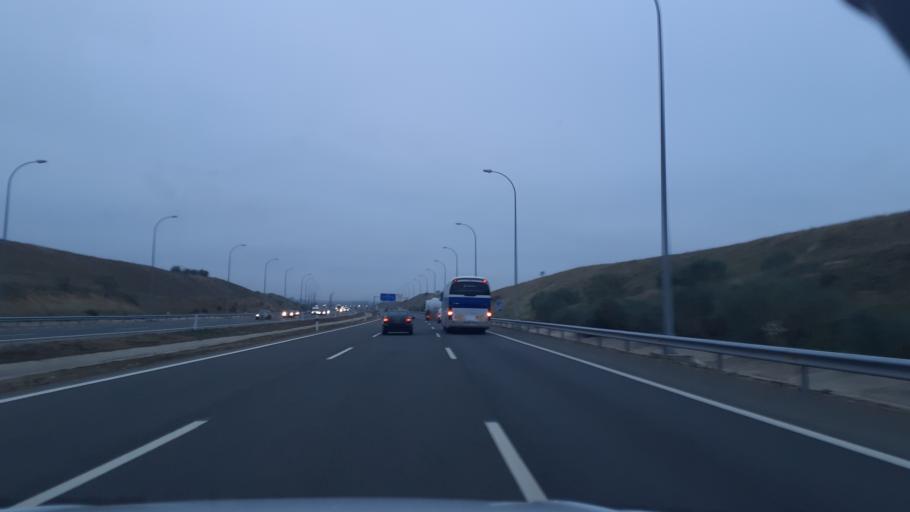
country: ES
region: Madrid
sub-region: Provincia de Madrid
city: Paracuellos de Jarama
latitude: 40.4895
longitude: -3.4966
